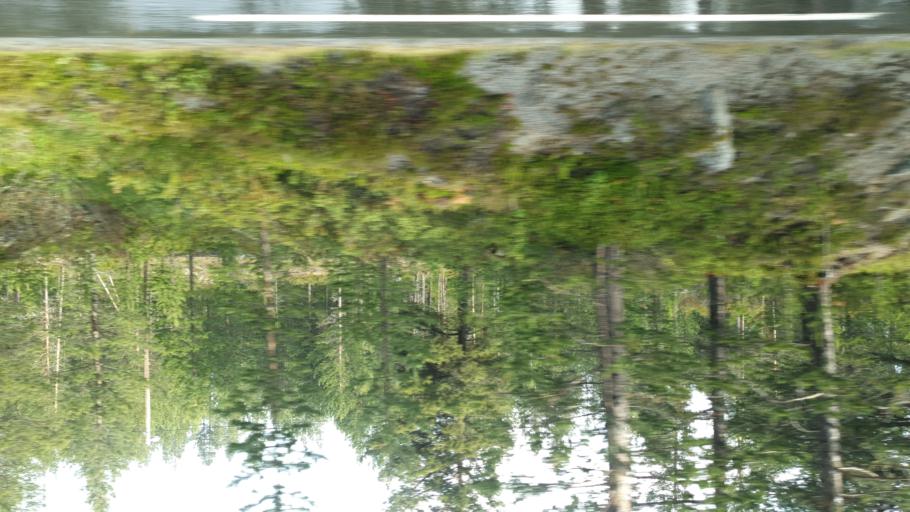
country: NO
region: Oppland
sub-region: Vaga
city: Vagamo
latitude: 61.8158
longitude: 8.9900
